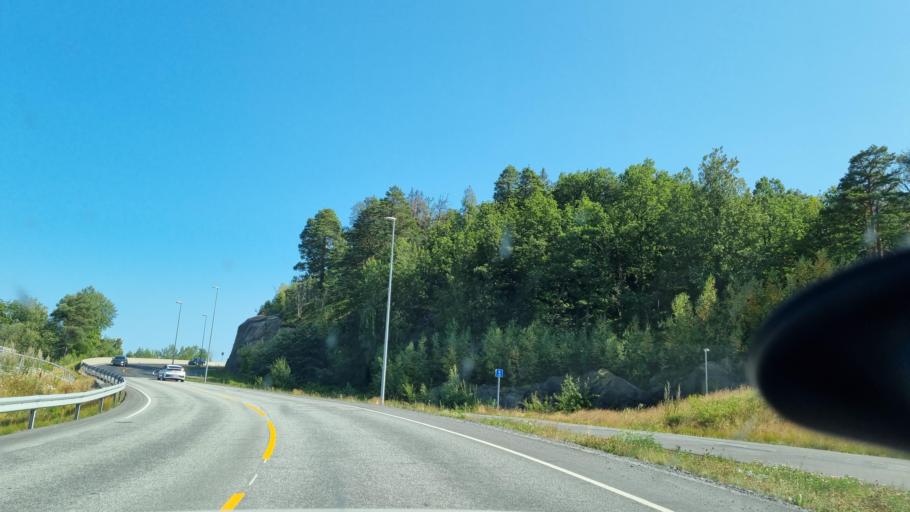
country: NO
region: Aust-Agder
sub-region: Arendal
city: Arendal
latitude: 58.4742
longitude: 8.8192
